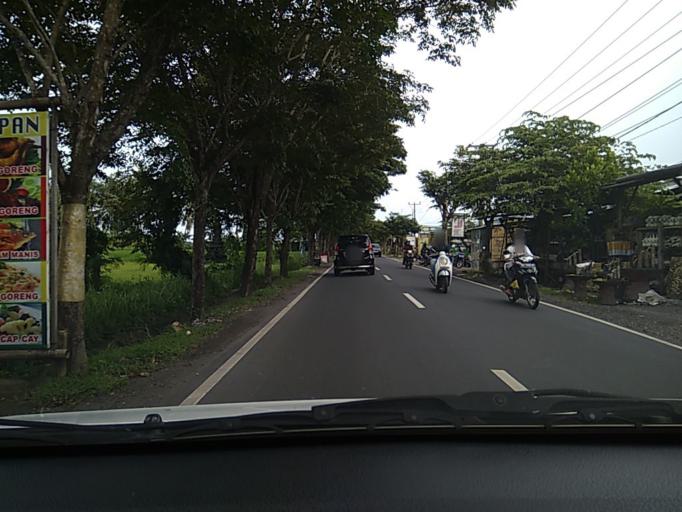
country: ID
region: Bali
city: Banjar Kerobokan
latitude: -8.6265
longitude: 115.1261
